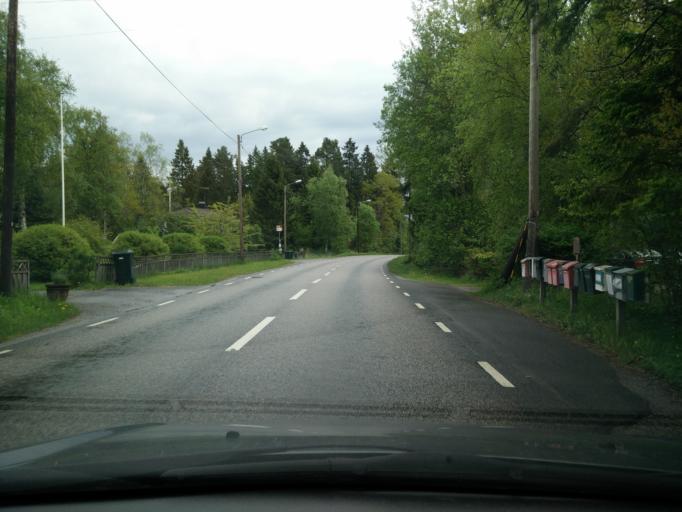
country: SE
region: Stockholm
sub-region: Norrtalje Kommun
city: Bjorko
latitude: 59.8073
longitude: 18.8880
